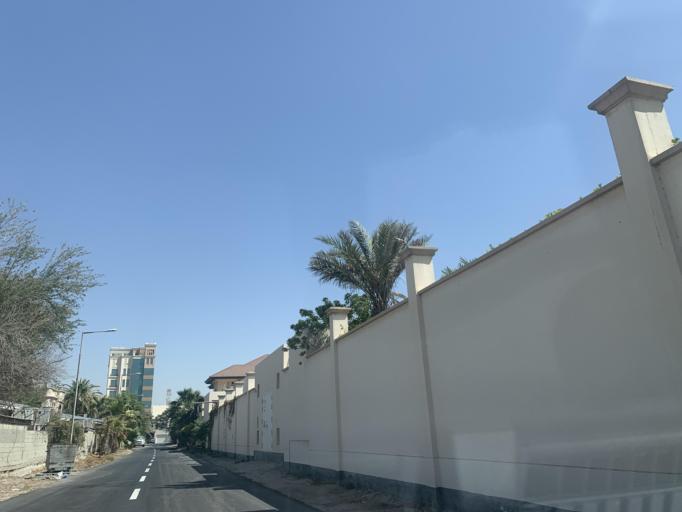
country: BH
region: Manama
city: Jidd Hafs
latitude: 26.2239
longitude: 50.5013
